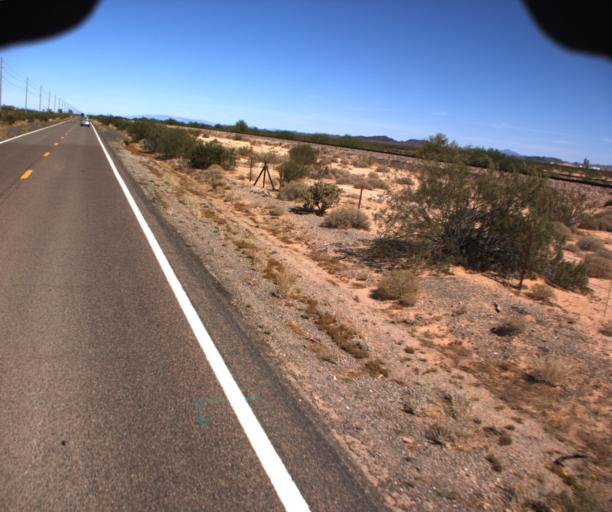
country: US
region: Arizona
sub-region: La Paz County
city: Salome
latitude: 33.8536
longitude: -113.9079
